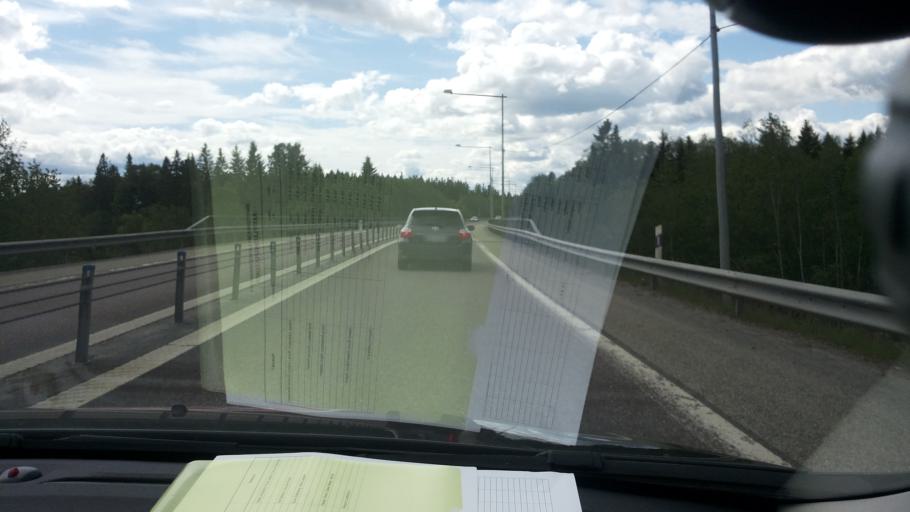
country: SE
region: Vaesternorrland
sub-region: Timra Kommun
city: Soraker
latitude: 62.5221
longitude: 17.4710
